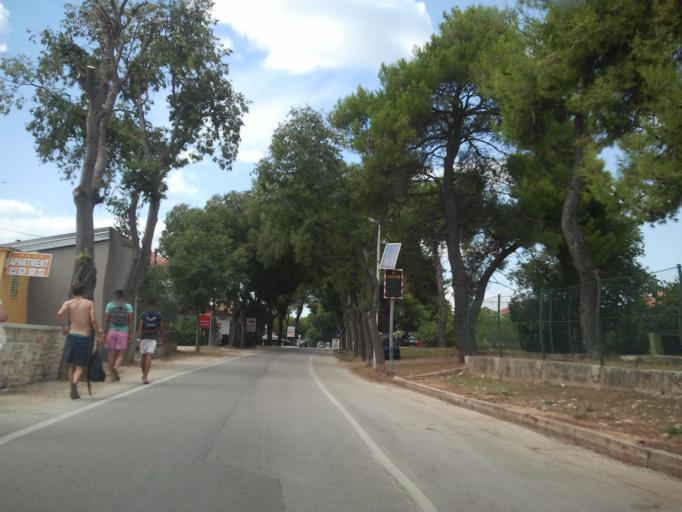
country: HR
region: Zadarska
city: Zadar
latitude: 44.1274
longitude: 15.2248
